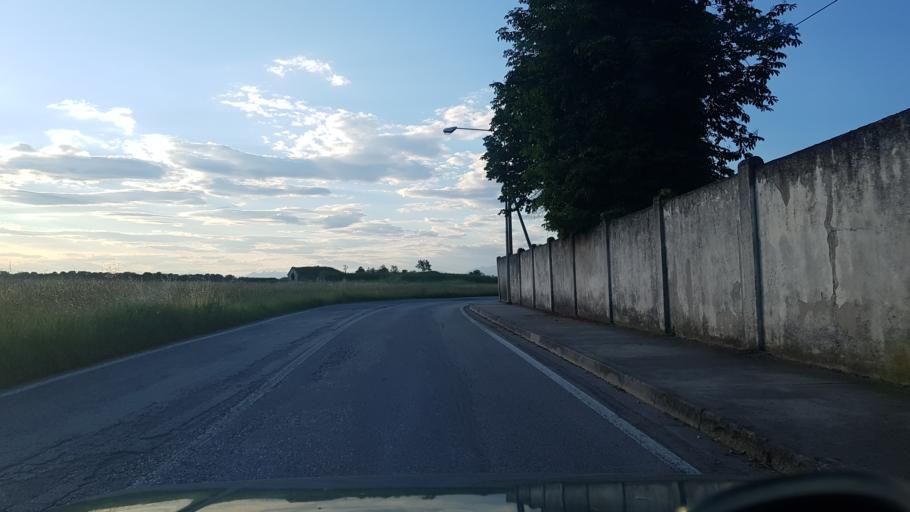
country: IT
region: Friuli Venezia Giulia
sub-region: Provincia di Udine
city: Sottoselva
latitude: 45.9085
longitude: 13.3179
